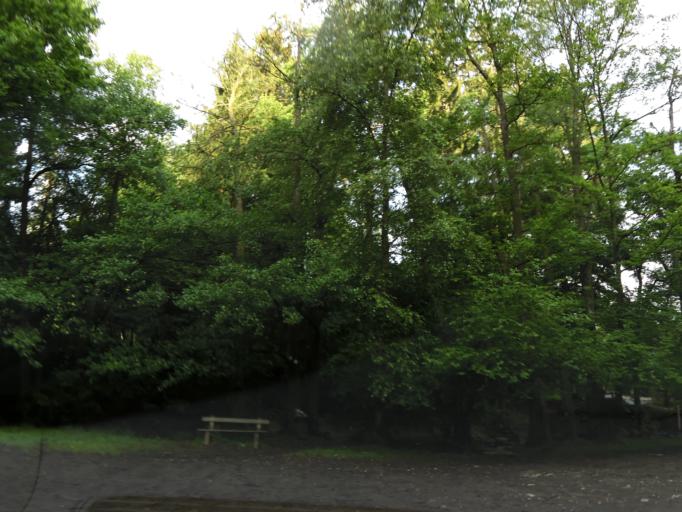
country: BE
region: Wallonia
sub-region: Province de Liege
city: Jalhay
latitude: 50.5080
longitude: 5.9604
